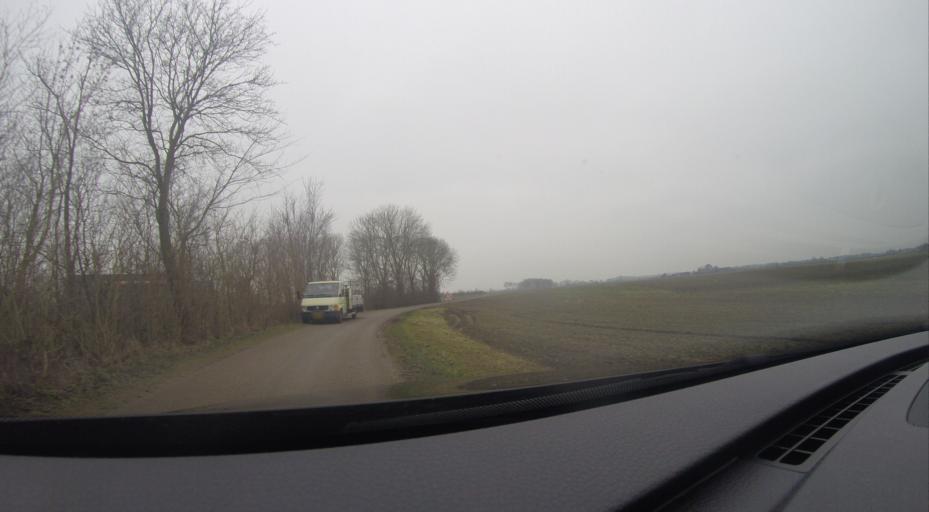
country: NL
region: Gelderland
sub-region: Gemeente Bronckhorst
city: Baak
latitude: 52.1006
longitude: 6.1998
